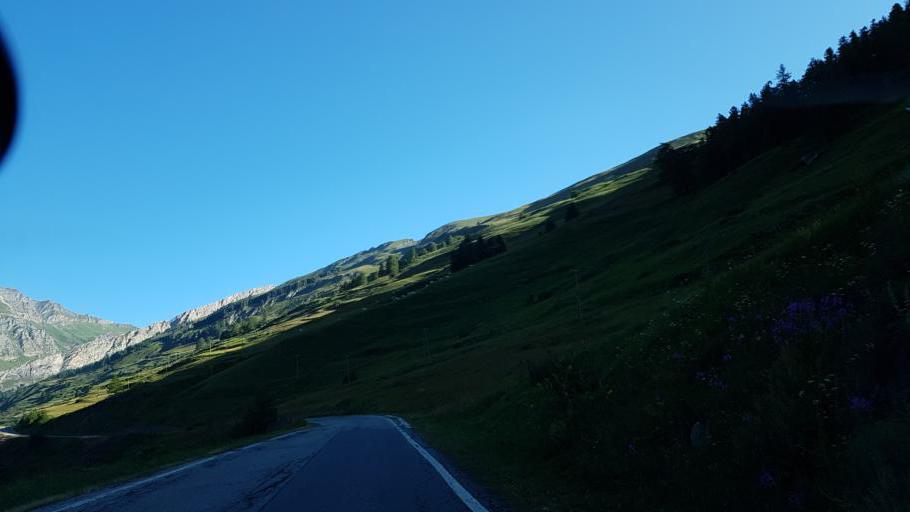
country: IT
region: Piedmont
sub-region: Provincia di Cuneo
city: Pontechianale
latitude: 44.6322
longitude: 7.0173
